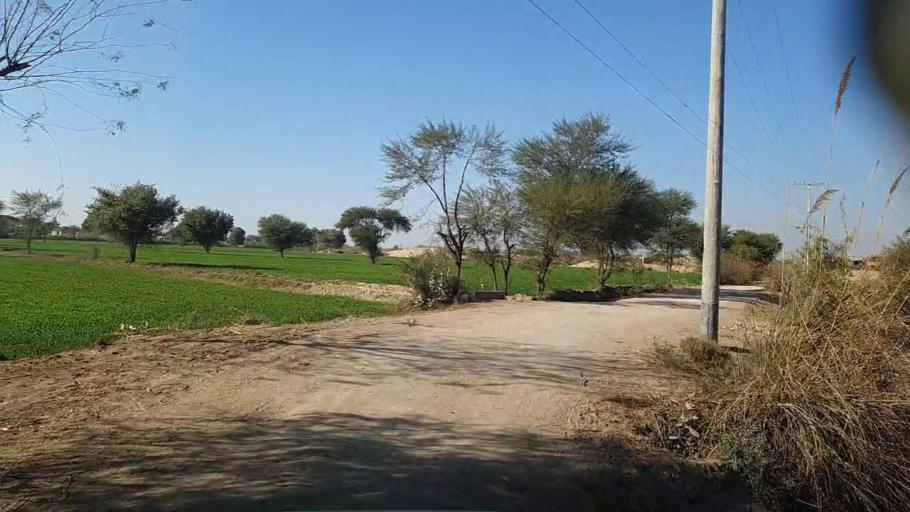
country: PK
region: Sindh
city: Khairpur
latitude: 27.9202
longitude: 69.7509
